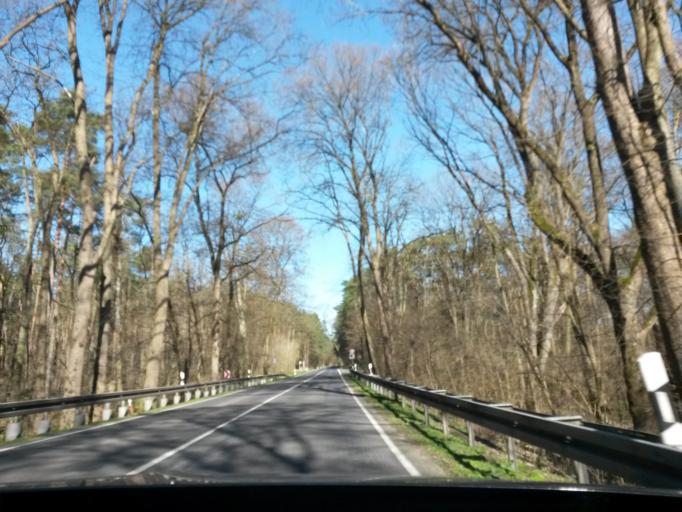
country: DE
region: Brandenburg
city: Grunheide
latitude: 52.4478
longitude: 13.8567
